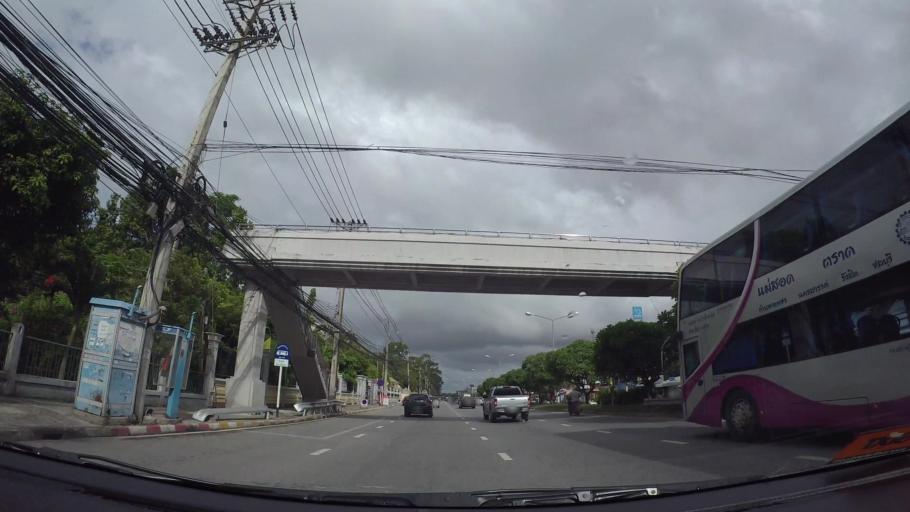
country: TH
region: Rayong
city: Rayong
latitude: 12.6834
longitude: 101.2323
